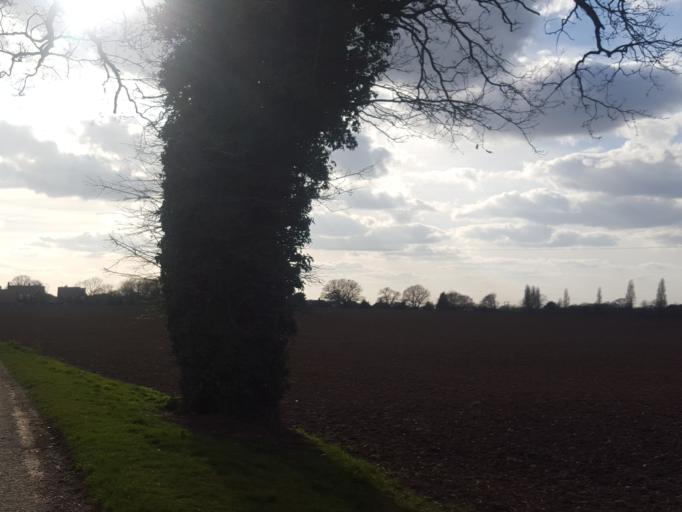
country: GB
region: England
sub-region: Essex
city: Little Clacton
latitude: 51.8499
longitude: 1.1254
